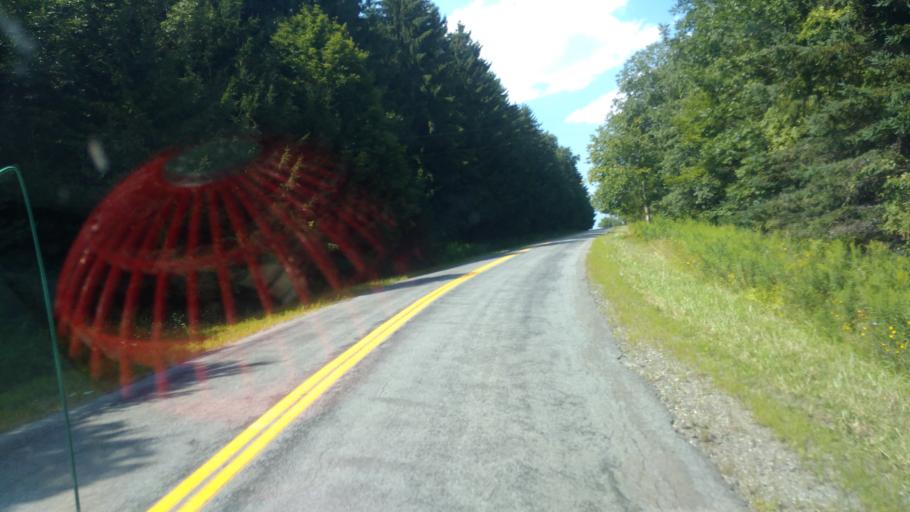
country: US
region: New York
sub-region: Steuben County
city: Canisteo
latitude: 42.3521
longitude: -77.5522
